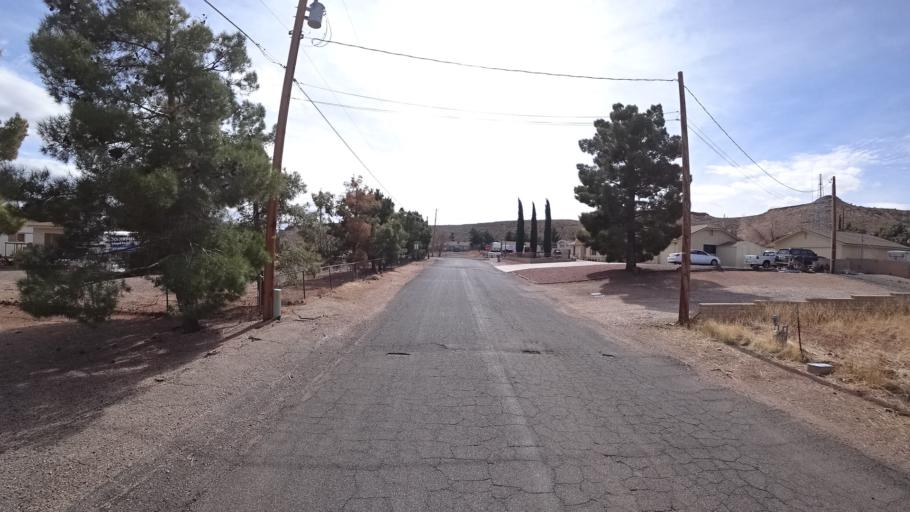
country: US
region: Arizona
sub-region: Mohave County
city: New Kingman-Butler
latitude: 35.2311
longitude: -114.0538
